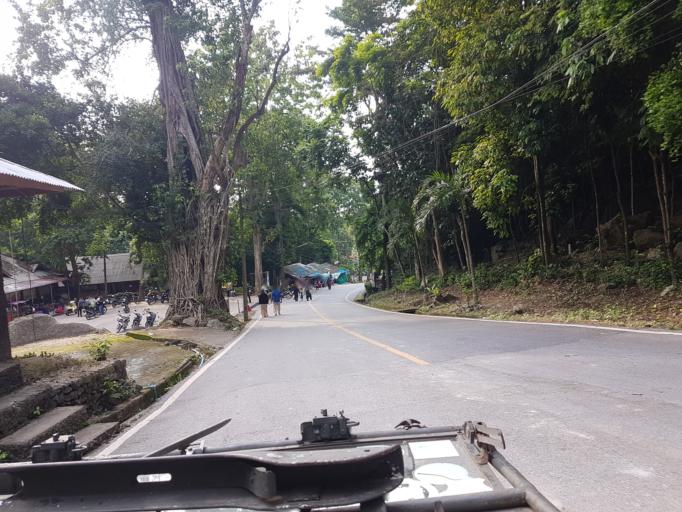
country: TH
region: Pattani
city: Khok Pho
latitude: 6.6573
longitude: 101.0955
